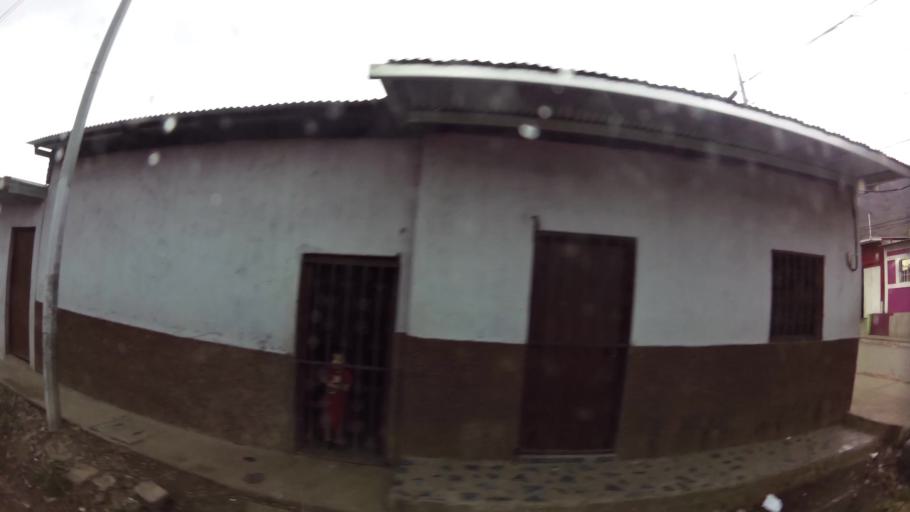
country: NI
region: Jinotega
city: Jinotega
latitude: 13.0980
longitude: -86.0060
